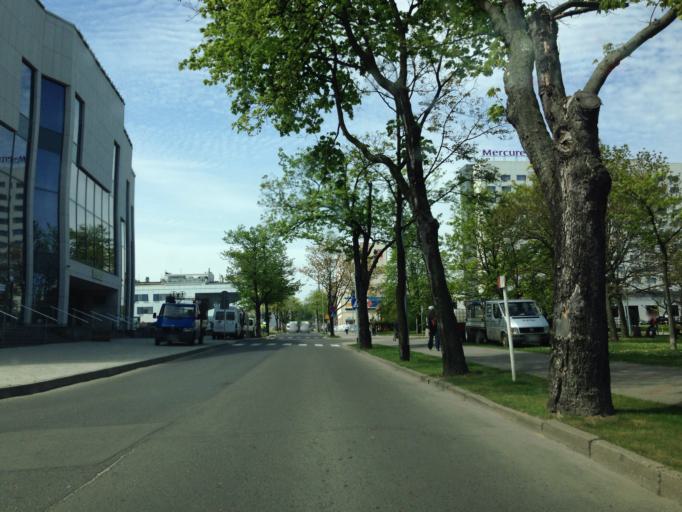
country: PL
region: Pomeranian Voivodeship
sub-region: Gdynia
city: Gdynia
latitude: 54.5170
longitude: 18.5463
